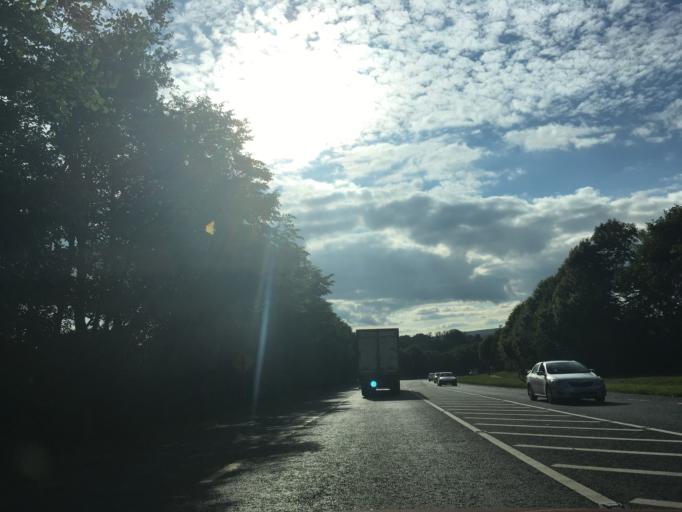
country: IE
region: Leinster
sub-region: Loch Garman
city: New Ross
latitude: 52.3818
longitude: -6.9396
